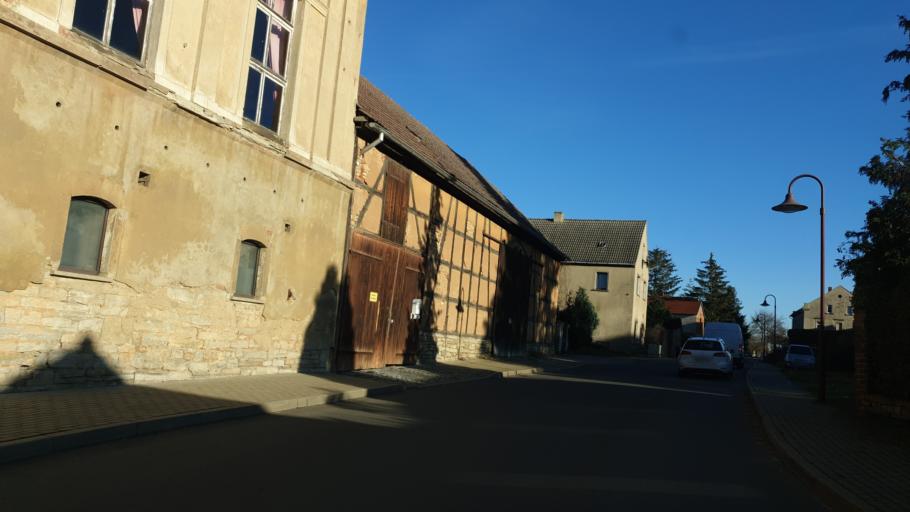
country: DE
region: Thuringia
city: Rauda
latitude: 50.9765
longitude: 11.9439
